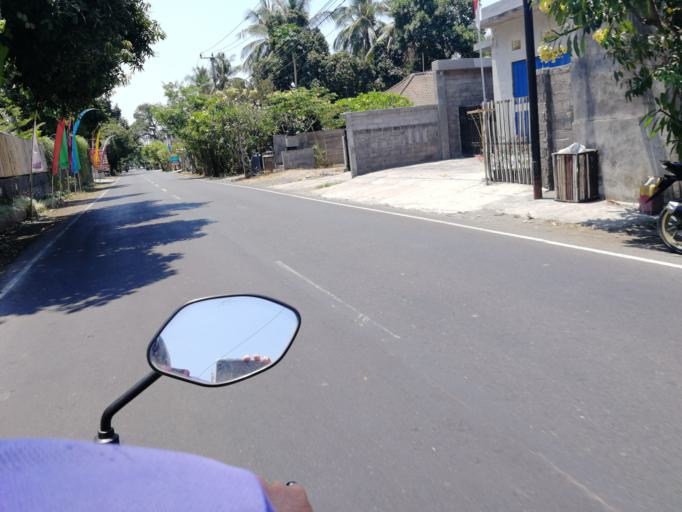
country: ID
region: Bali
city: Banjar Trunyan
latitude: -8.1417
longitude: 115.3901
